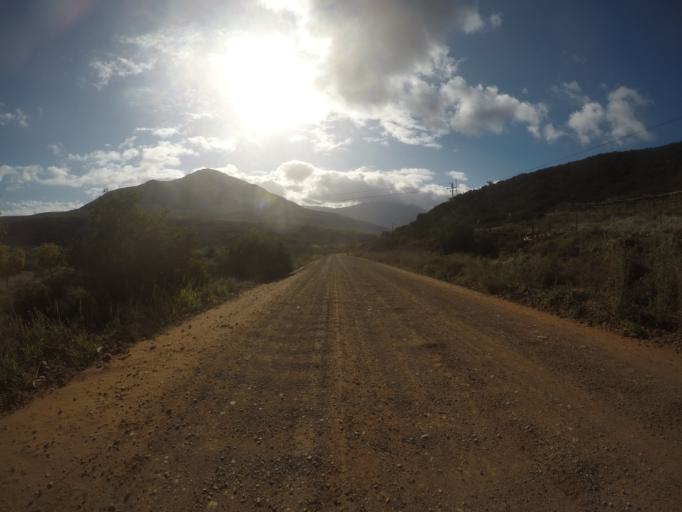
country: ZA
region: Western Cape
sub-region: West Coast District Municipality
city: Clanwilliam
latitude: -32.3635
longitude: 18.9429
